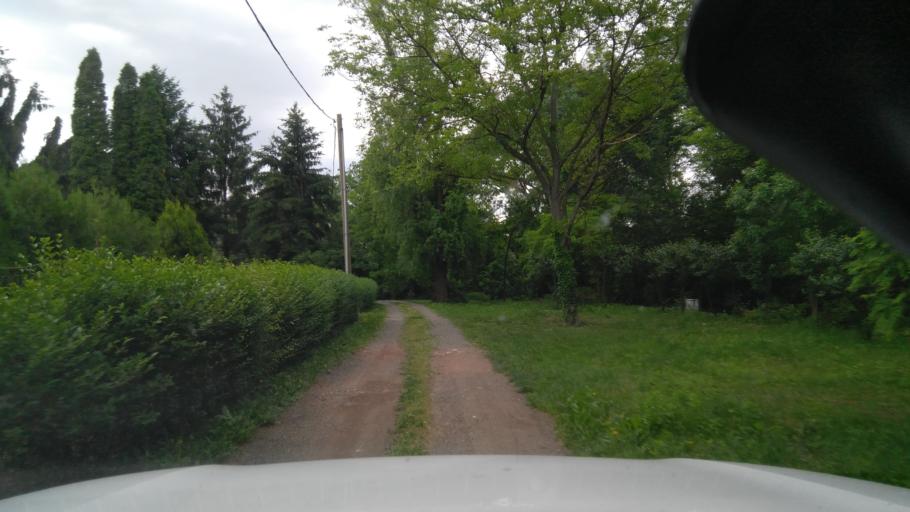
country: HU
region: Bekes
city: Bekescsaba
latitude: 46.6721
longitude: 21.1864
